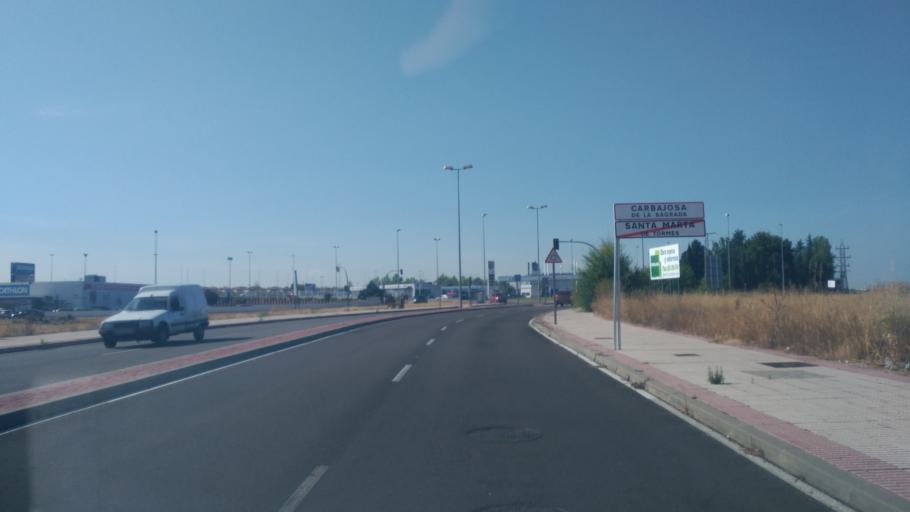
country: ES
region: Castille and Leon
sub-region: Provincia de Salamanca
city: Santa Marta de Tormes
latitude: 40.9478
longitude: -5.6417
